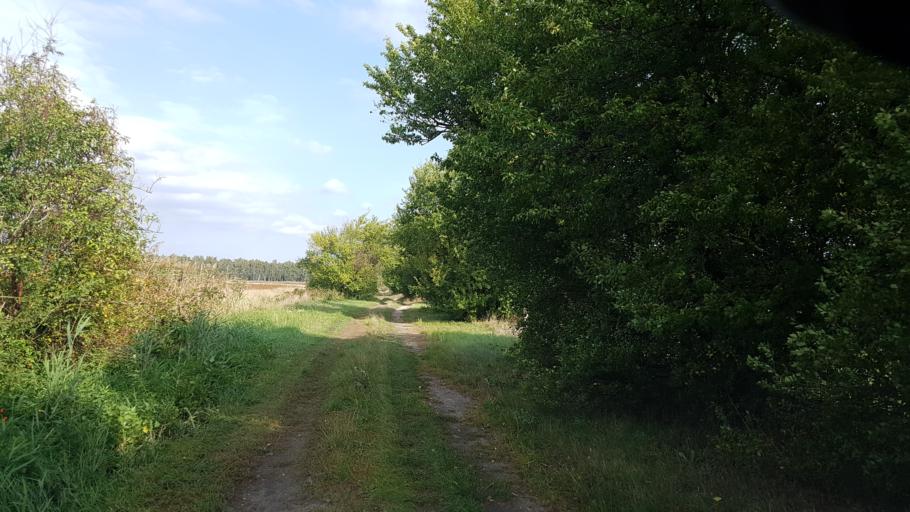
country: DE
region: Brandenburg
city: Ruckersdorf
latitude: 51.5406
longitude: 13.6217
